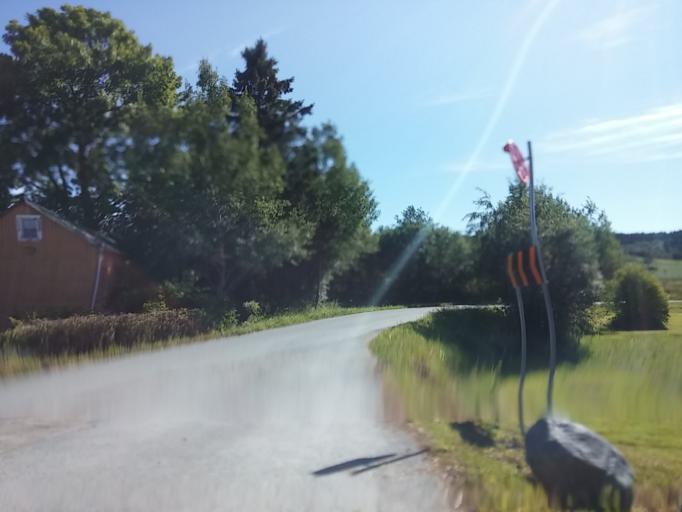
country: NO
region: Sor-Trondelag
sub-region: Malvik
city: Malvik
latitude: 63.4323
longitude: 10.7287
